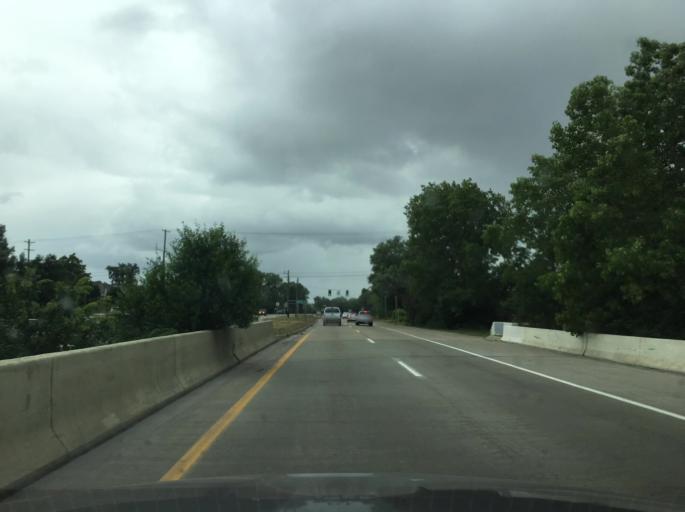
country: US
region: Michigan
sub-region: Macomb County
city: Mount Clemens
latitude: 42.5705
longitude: -82.8624
